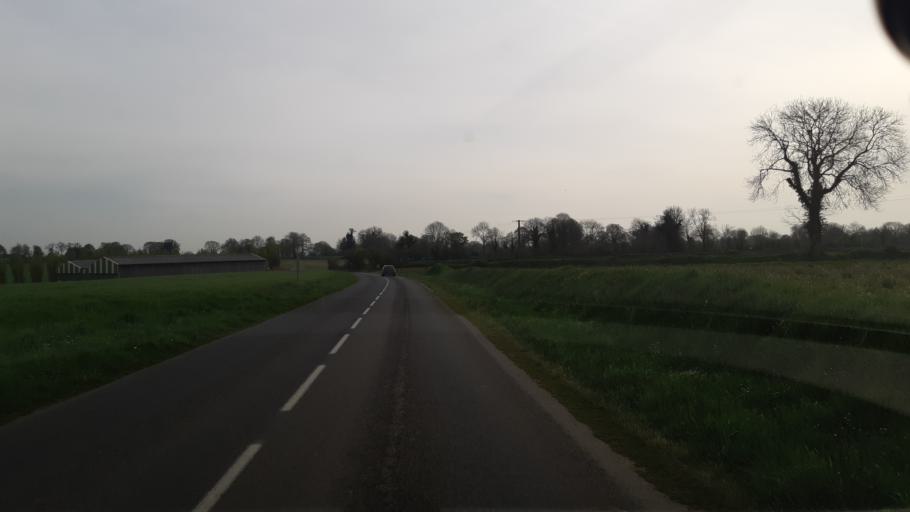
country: FR
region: Lower Normandy
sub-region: Departement de la Manche
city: Gavray
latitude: 48.9504
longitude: -1.3292
